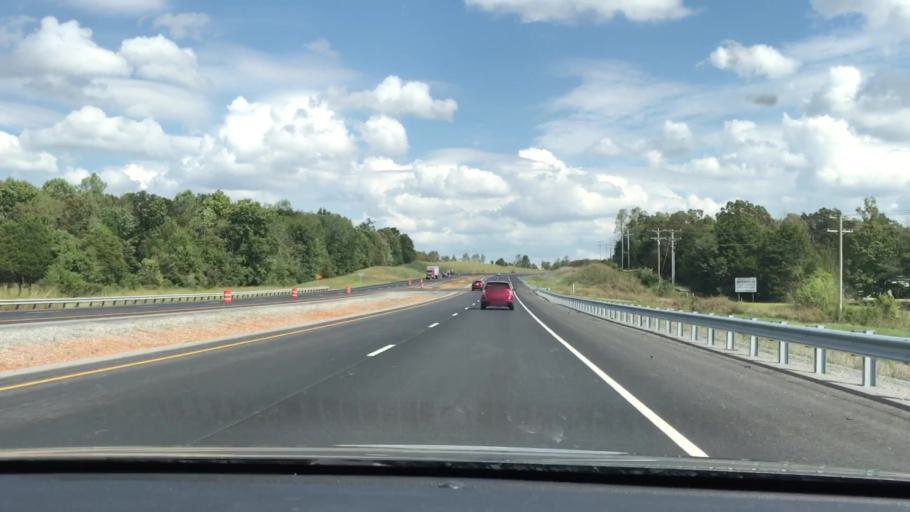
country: US
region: Kentucky
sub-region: Trigg County
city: Cadiz
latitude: 36.8550
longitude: -87.8153
